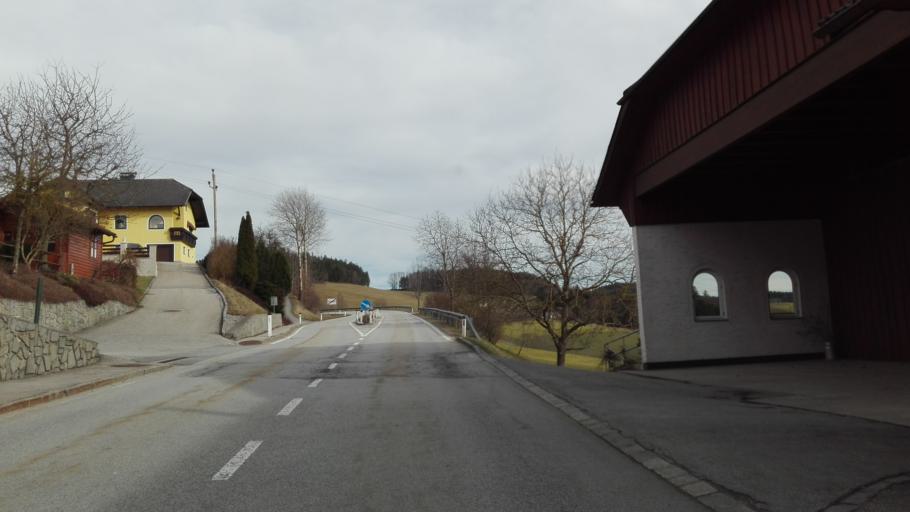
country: AT
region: Upper Austria
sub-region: Politischer Bezirk Rohrbach
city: Schlaegl
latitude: 48.6038
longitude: 13.9186
